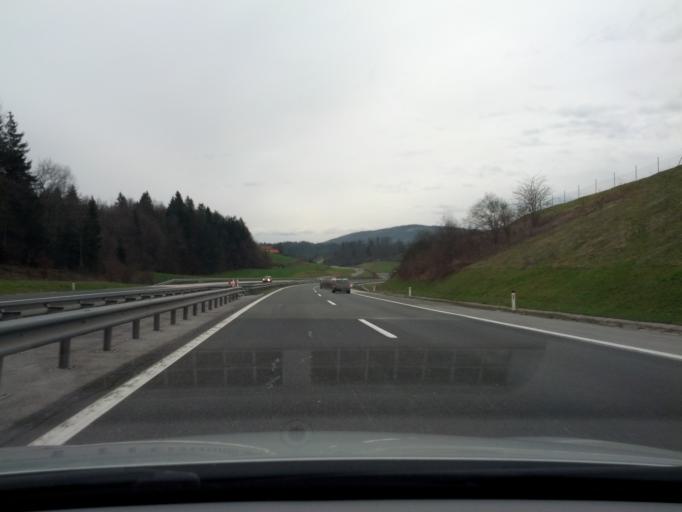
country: SI
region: Trebnje
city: Trebnje
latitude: 45.9241
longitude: 14.9355
